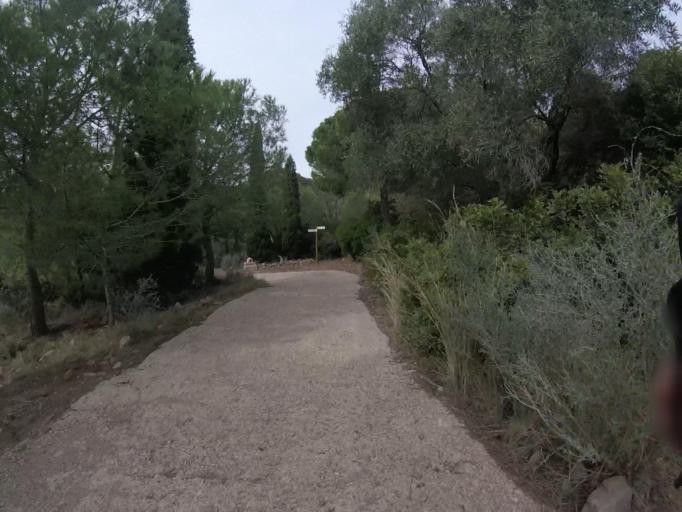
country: ES
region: Valencia
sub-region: Provincia de Castello
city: Benicassim
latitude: 40.0759
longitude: 0.0359
